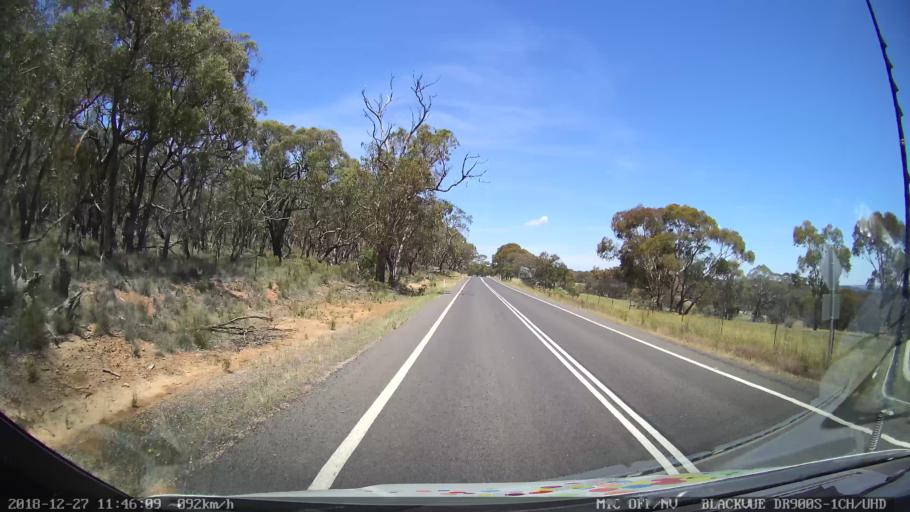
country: AU
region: New South Wales
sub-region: Bathurst Regional
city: Perthville
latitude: -33.5881
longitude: 149.4616
